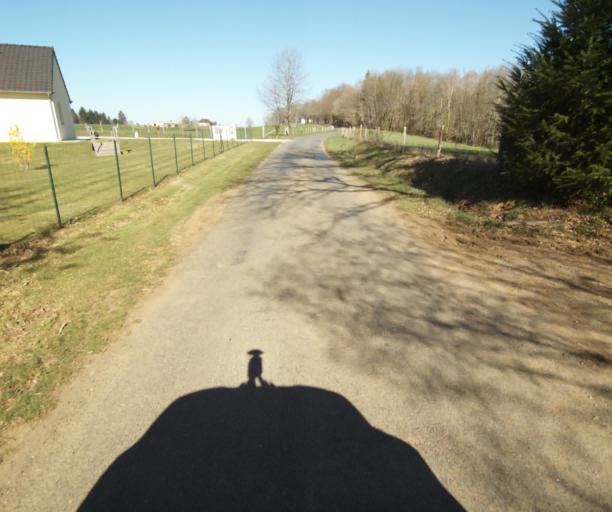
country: FR
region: Limousin
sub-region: Departement de la Correze
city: Seilhac
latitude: 45.3906
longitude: 1.7535
